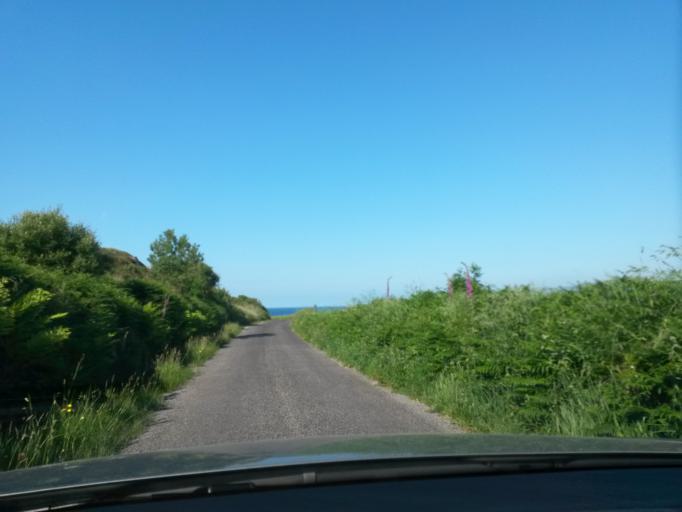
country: IE
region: Munster
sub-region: Ciarrai
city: Kenmare
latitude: 51.7887
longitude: -9.8167
